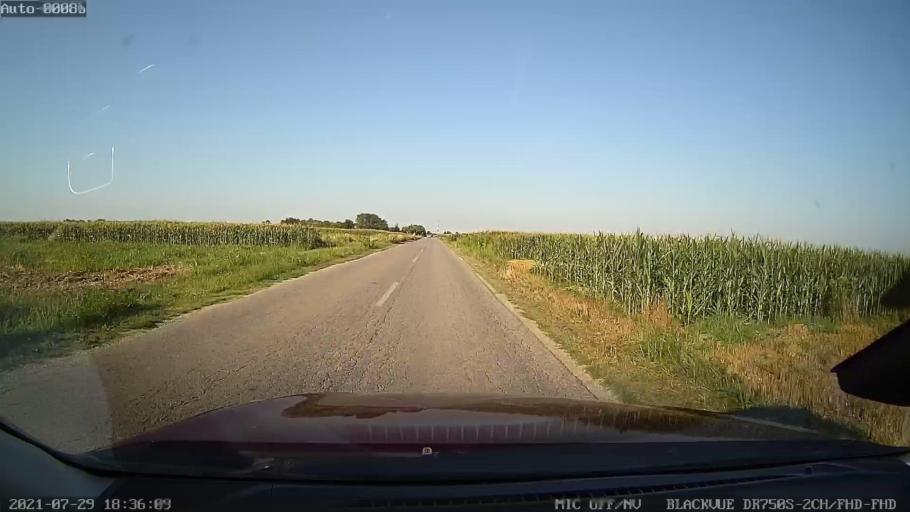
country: HR
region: Varazdinska
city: Vinica
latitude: 46.3153
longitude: 16.1814
